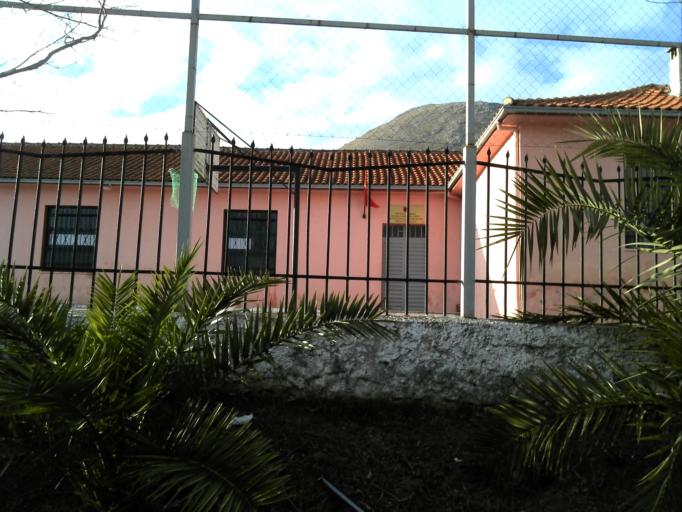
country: AL
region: Shkoder
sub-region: Rrethi i Shkodres
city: Berdica e Madhe
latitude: 42.0335
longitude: 19.4773
